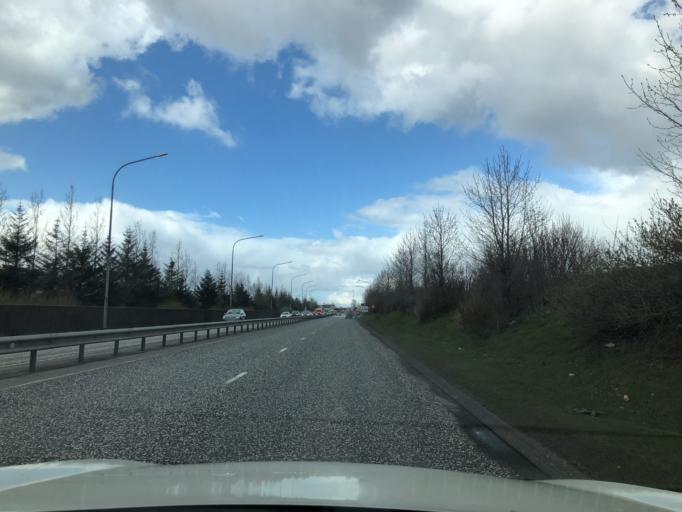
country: IS
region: Capital Region
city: Hafnarfjoerdur
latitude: 64.0710
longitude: -21.9387
